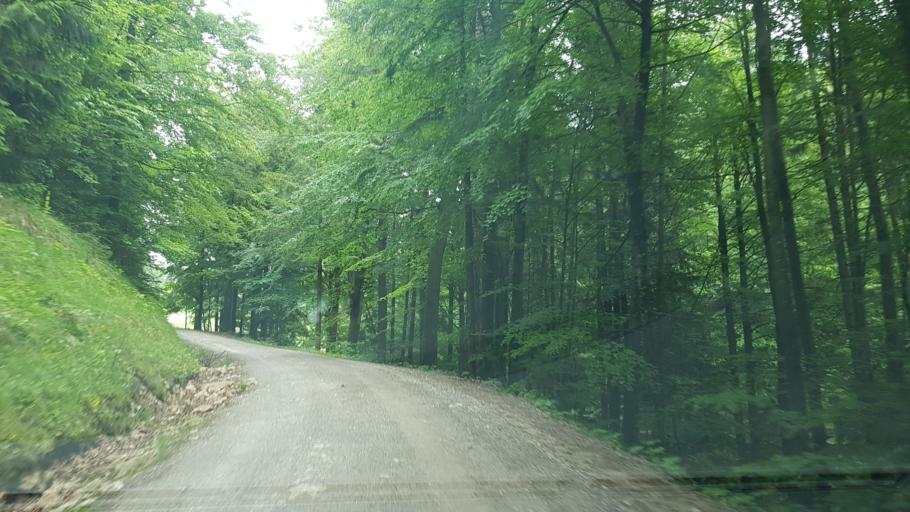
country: SI
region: Dobrna
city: Dobrna
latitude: 46.3844
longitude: 15.2189
